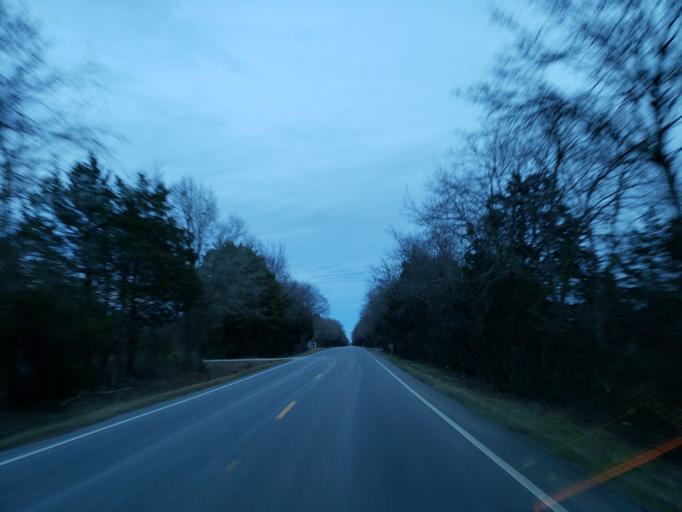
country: US
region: Alabama
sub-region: Sumter County
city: Livingston
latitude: 32.8113
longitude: -88.2458
